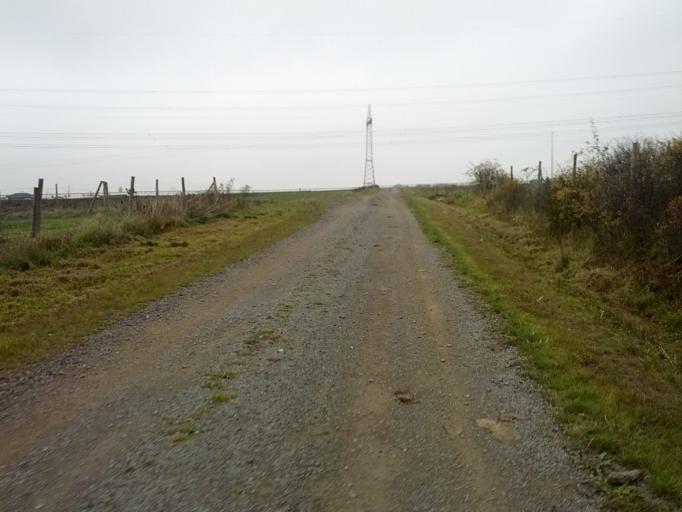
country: DE
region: Thuringia
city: Seebach
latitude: 50.9896
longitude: 10.4400
